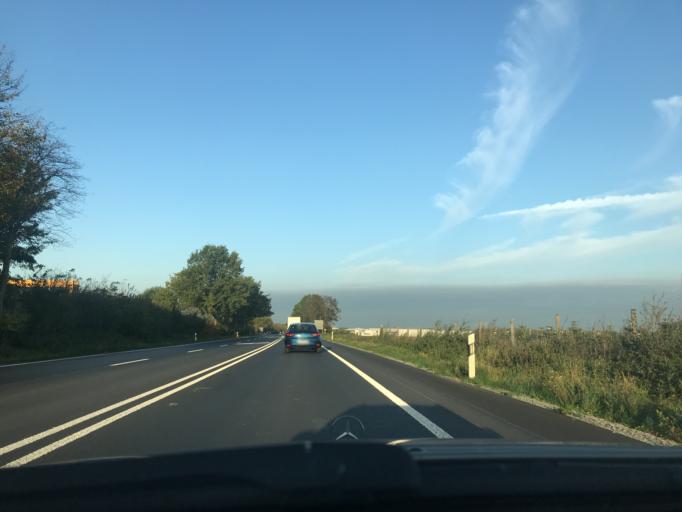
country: DE
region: North Rhine-Westphalia
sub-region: Regierungsbezirk Arnsberg
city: Bad Sassendorf
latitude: 51.5562
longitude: 8.1548
